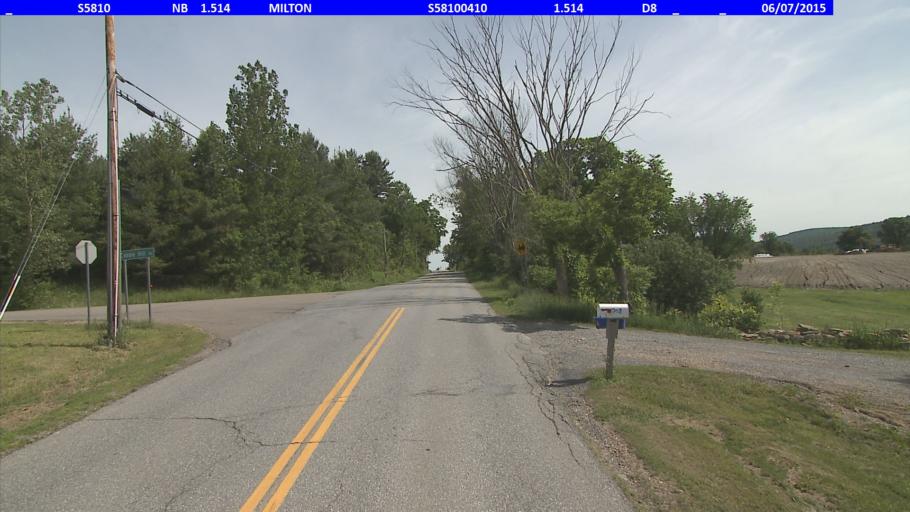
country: US
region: Vermont
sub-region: Chittenden County
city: Milton
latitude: 44.6030
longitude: -73.1260
